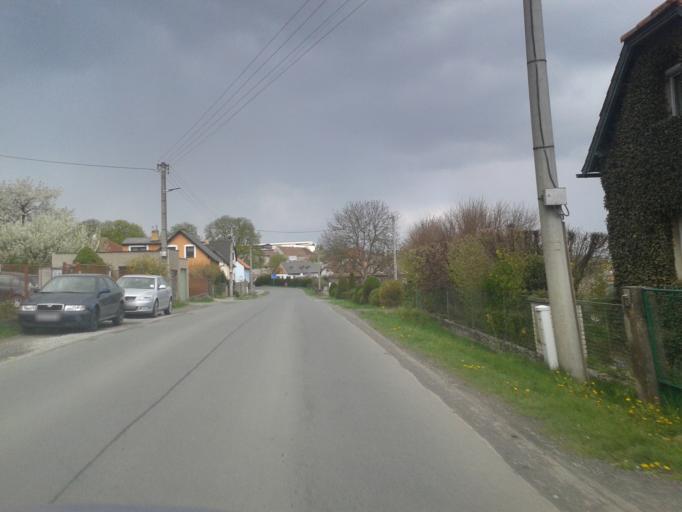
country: CZ
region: Central Bohemia
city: Hudlice
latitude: 49.9596
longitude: 13.9777
